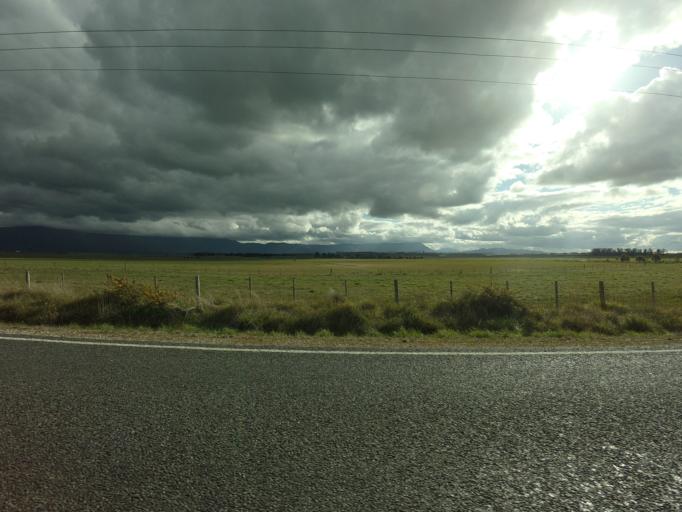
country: AU
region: Tasmania
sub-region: Northern Midlands
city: Longford
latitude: -41.7457
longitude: 147.0823
